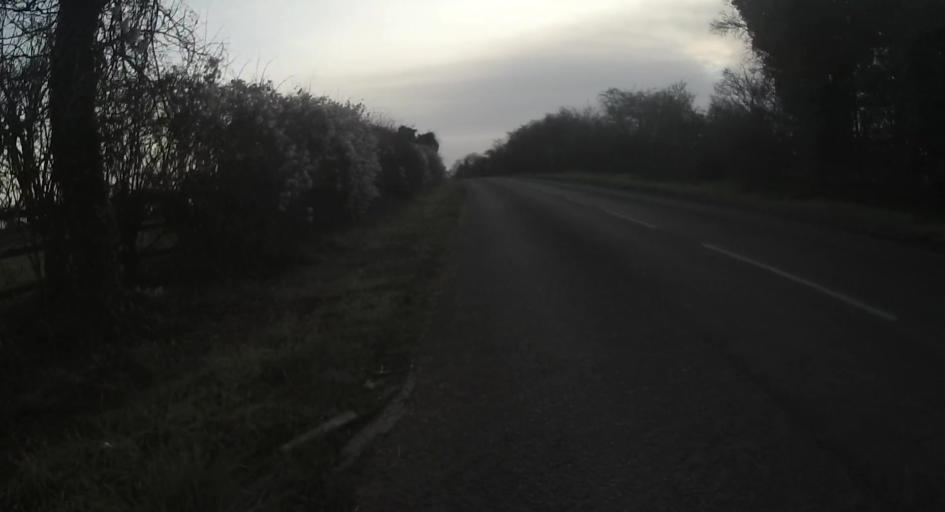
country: GB
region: England
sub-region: Hampshire
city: Overton
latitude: 51.2549
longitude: -1.3302
